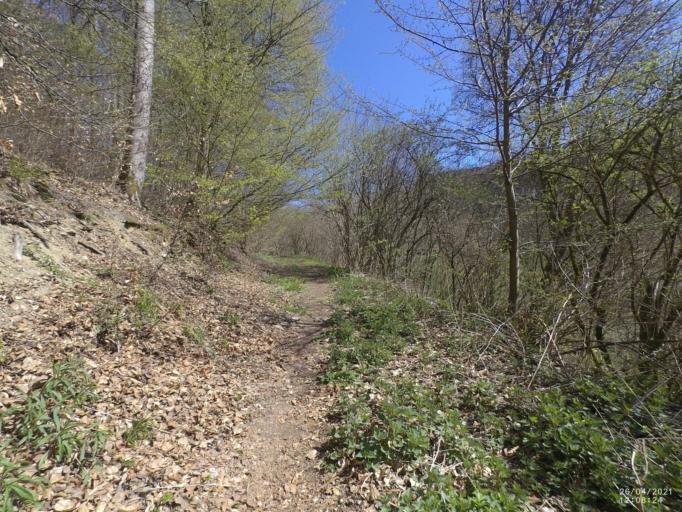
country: DE
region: Rheinland-Pfalz
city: Hohr-Grenzhausen
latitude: 50.4279
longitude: 7.6485
